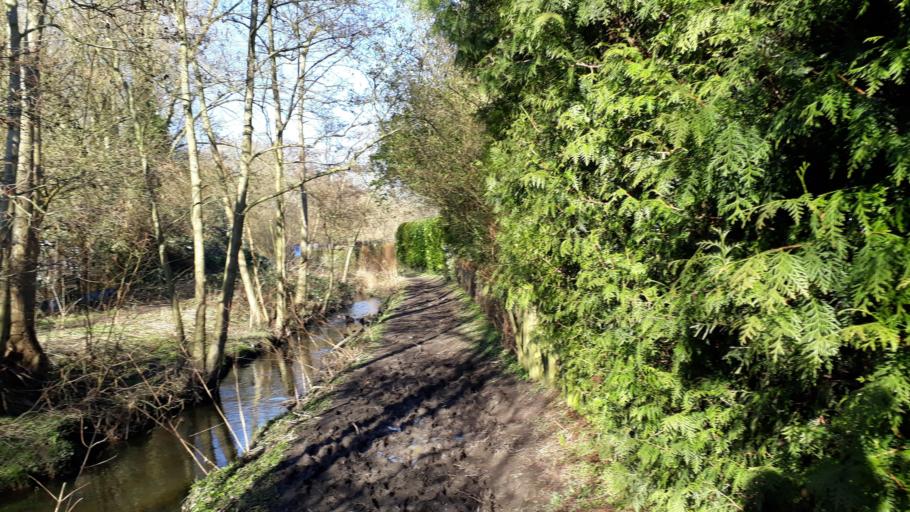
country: DE
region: Hamburg
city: Steilshoop
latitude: 53.5913
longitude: 10.0648
